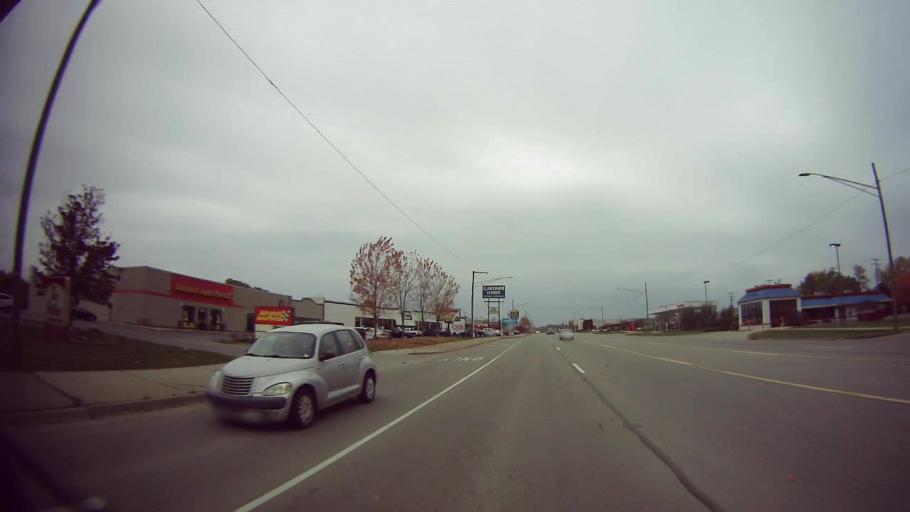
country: US
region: Michigan
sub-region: Oakland County
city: Waterford
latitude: 42.6906
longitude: -83.3867
